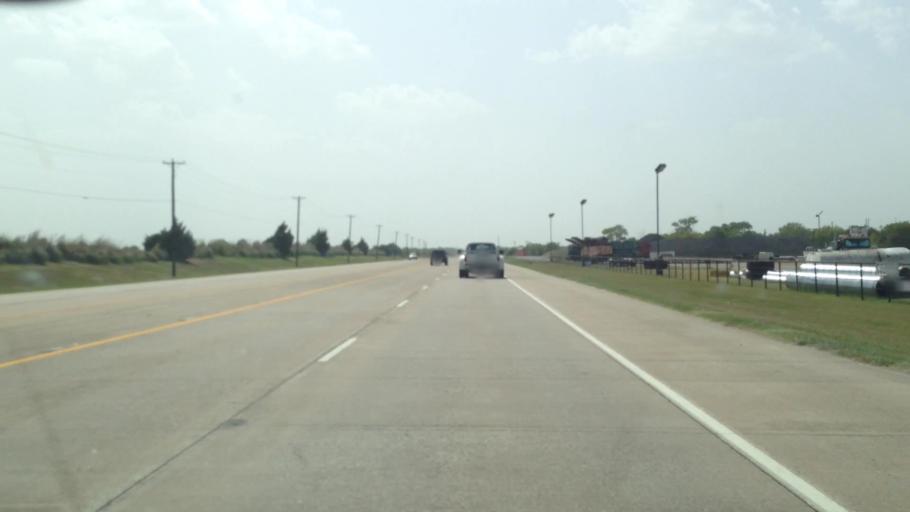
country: US
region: Texas
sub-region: Collin County
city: Princeton
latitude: 33.1670
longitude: -96.4584
